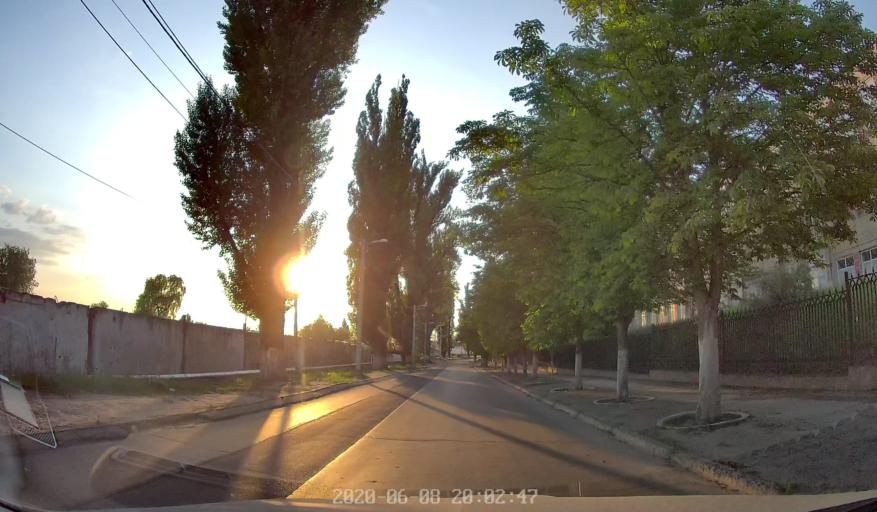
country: MD
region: Chisinau
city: Chisinau
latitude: 47.0106
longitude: 28.8818
